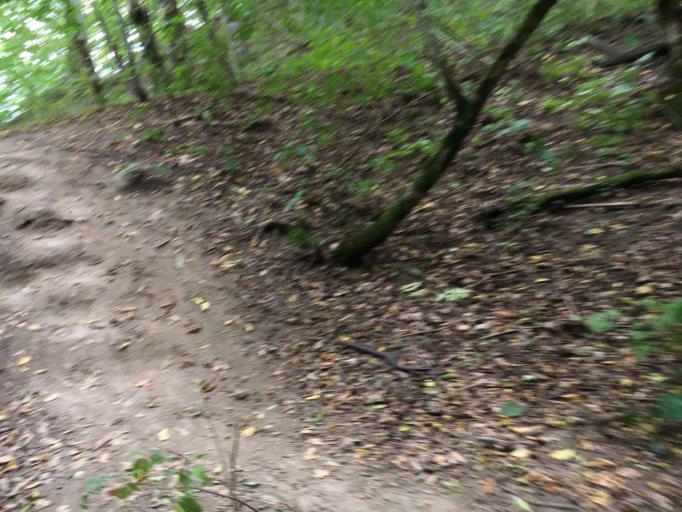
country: RU
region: Krasnodarskiy
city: Tuapse
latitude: 44.2530
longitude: 39.2285
